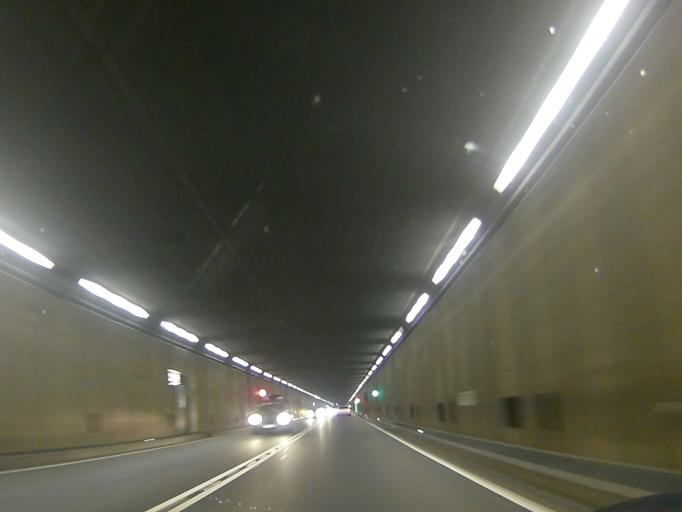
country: CH
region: Ticino
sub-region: Leventina District
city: Airolo
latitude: 46.5595
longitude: 8.5789
